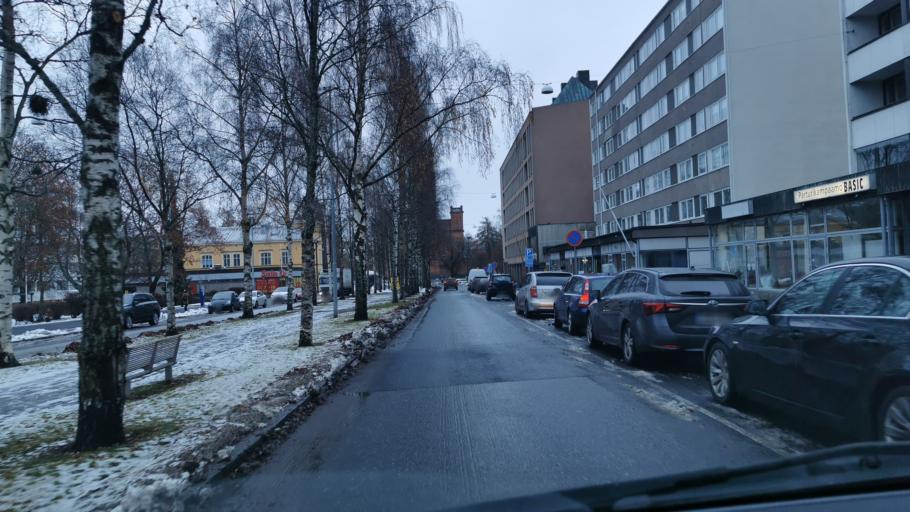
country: FI
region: Ostrobothnia
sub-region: Vaasa
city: Vaasa
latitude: 63.0967
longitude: 21.6082
